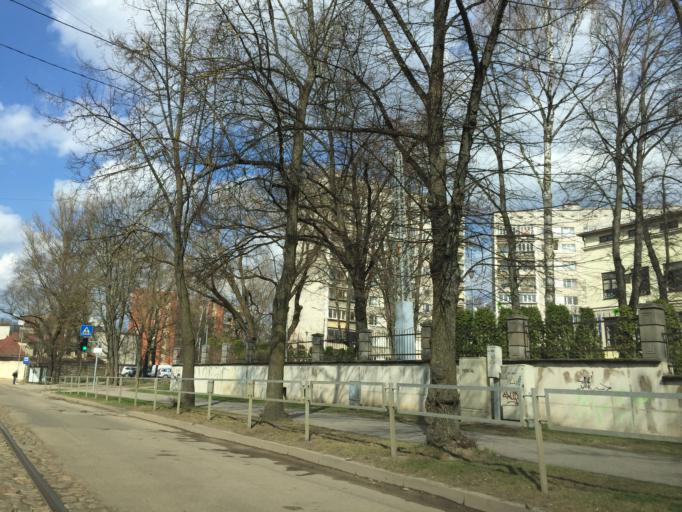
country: LV
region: Riga
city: Riga
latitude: 56.9327
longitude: 24.1606
